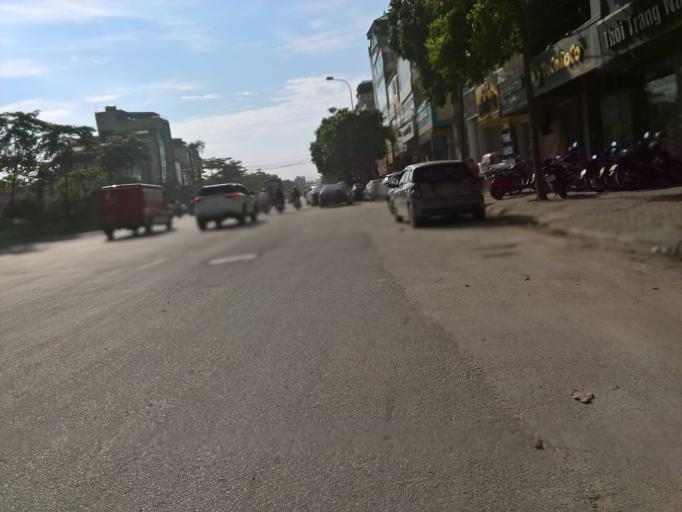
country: VN
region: Ha Noi
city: Troi
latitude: 21.0548
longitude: 105.7323
